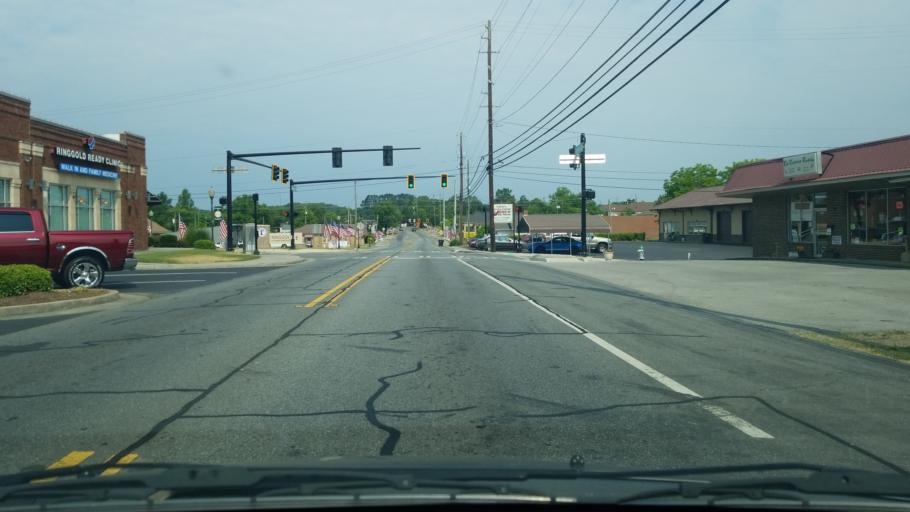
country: US
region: Georgia
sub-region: Catoosa County
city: Ringgold
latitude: 34.9168
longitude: -85.1124
